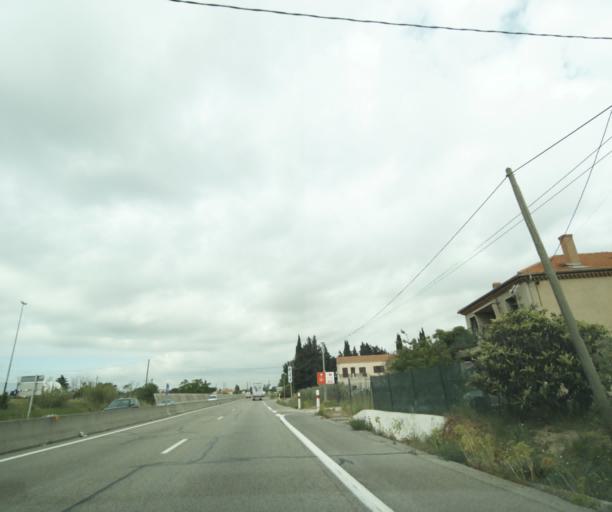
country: FR
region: Provence-Alpes-Cote d'Azur
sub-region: Departement des Bouches-du-Rhone
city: Rognac
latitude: 43.4929
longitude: 5.2288
